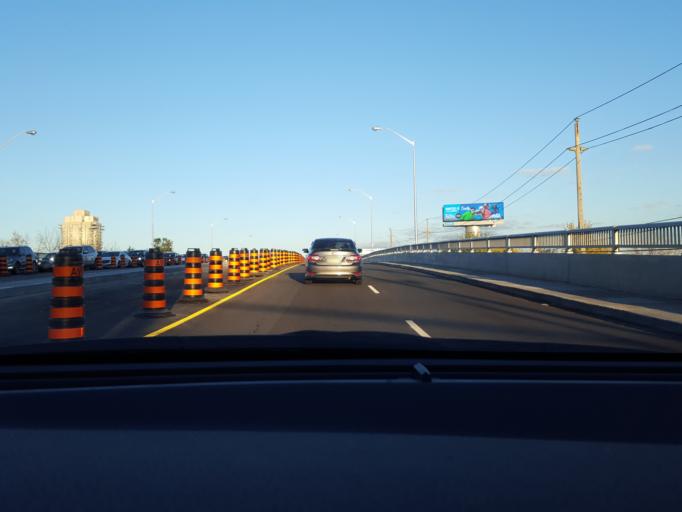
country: CA
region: Ontario
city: Willowdale
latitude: 43.7535
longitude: -79.3570
